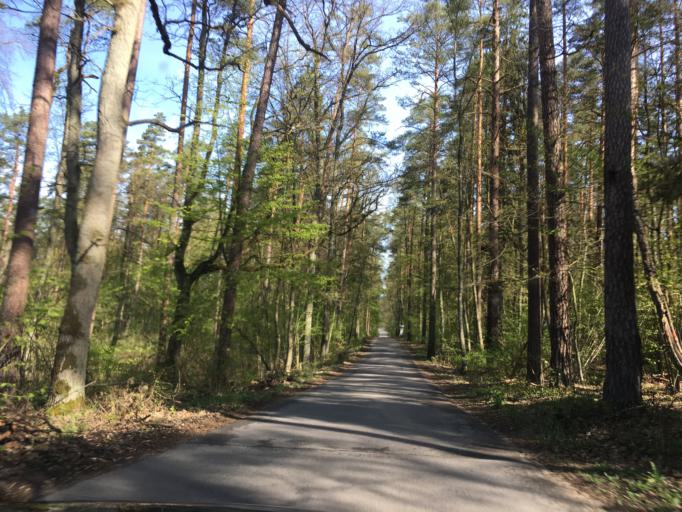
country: PL
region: Warmian-Masurian Voivodeship
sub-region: Powiat piski
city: Ruciane-Nida
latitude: 53.6805
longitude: 21.5894
